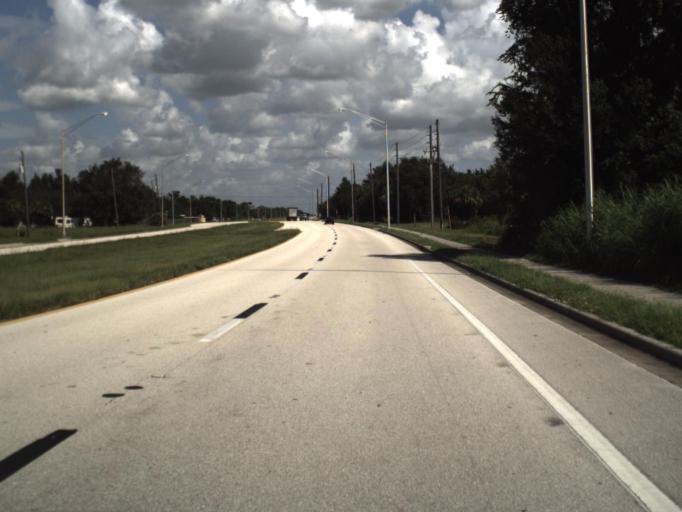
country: US
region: Florida
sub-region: Charlotte County
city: Cleveland
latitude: 26.9838
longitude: -81.9590
